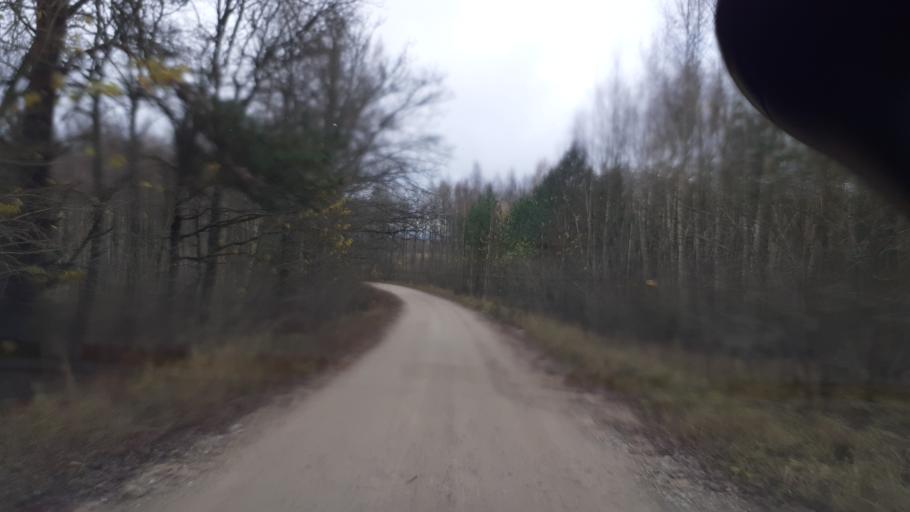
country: LV
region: Kuldigas Rajons
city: Kuldiga
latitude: 57.0362
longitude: 21.8794
